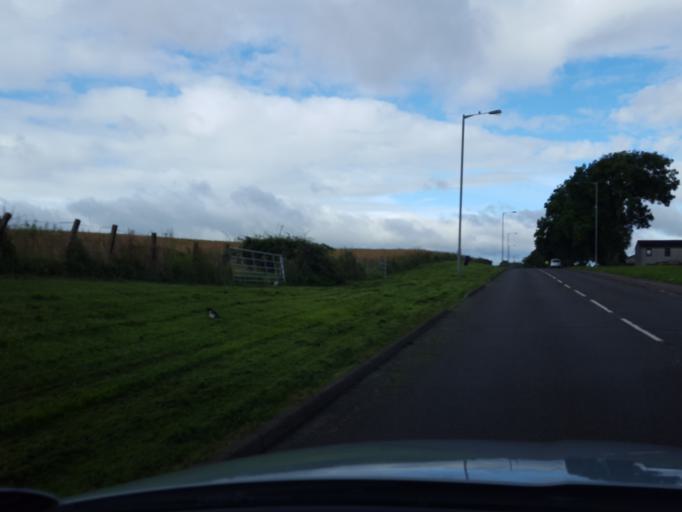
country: GB
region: Scotland
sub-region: Falkirk
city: Bo'ness
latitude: 56.0024
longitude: -3.6127
